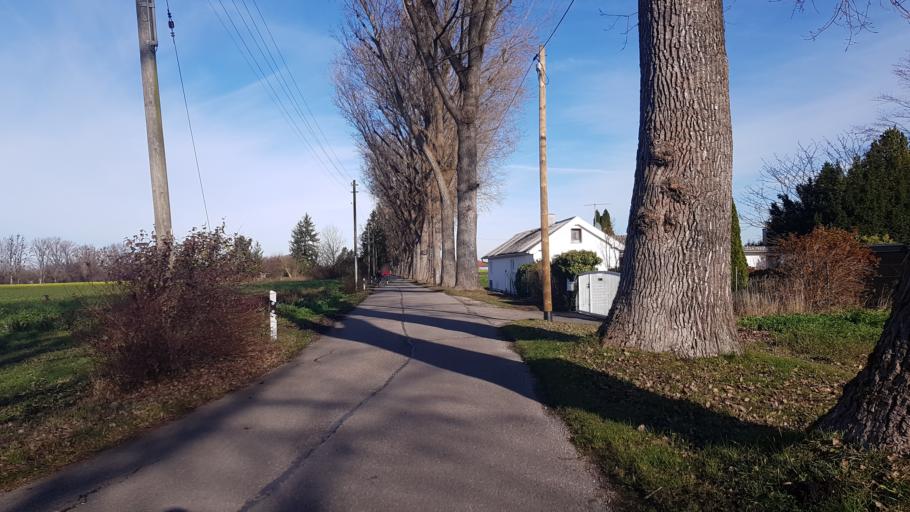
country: DE
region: Bavaria
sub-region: Upper Bavaria
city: Karlsfeld
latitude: 48.2056
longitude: 11.5154
